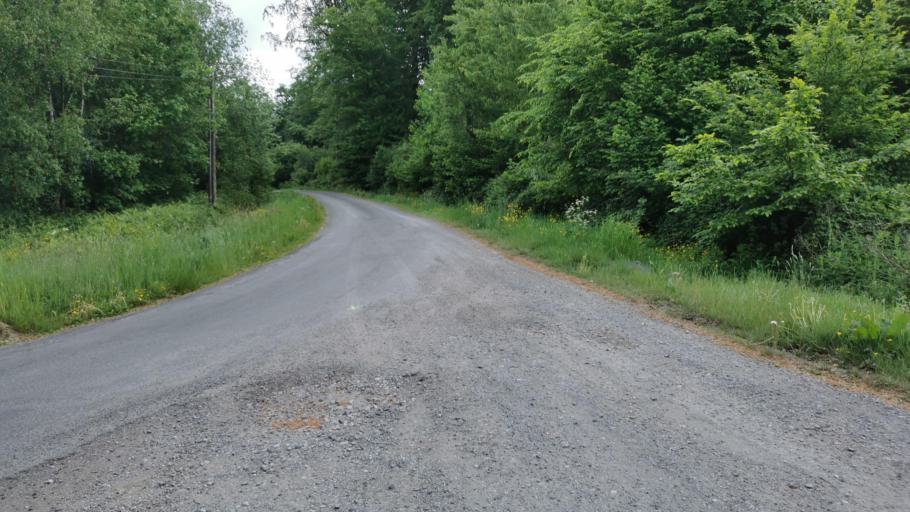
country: FR
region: Nord-Pas-de-Calais
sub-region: Departement du Nord
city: Trelon
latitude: 50.0359
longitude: 4.0955
